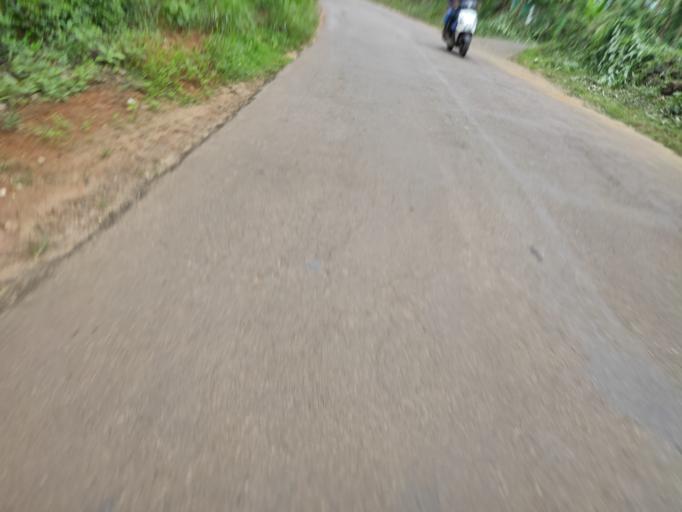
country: IN
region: Kerala
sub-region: Malappuram
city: Manjeri
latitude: 11.2386
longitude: 76.2860
